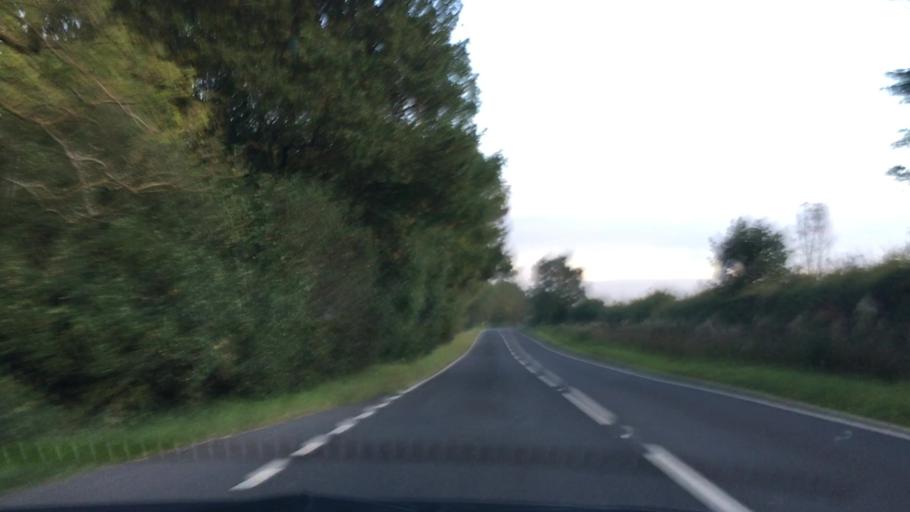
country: GB
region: England
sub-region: North East Lincolnshire
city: Wold Newton
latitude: 53.4728
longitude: -0.1114
